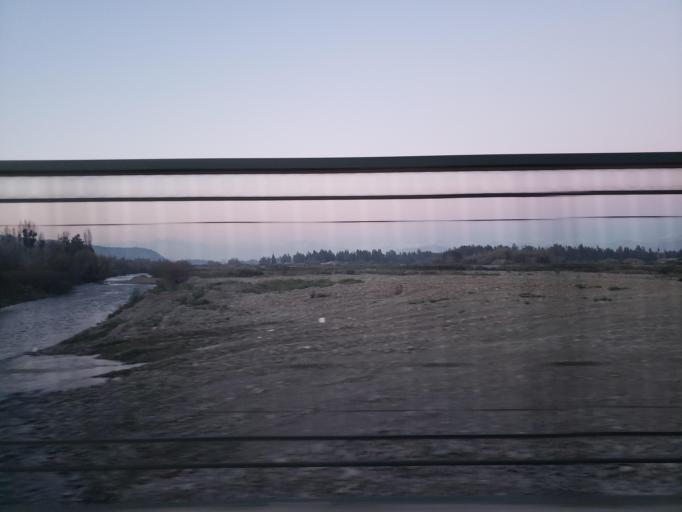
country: CL
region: Santiago Metropolitan
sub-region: Provincia de Talagante
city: El Monte
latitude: -33.6812
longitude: -70.9764
